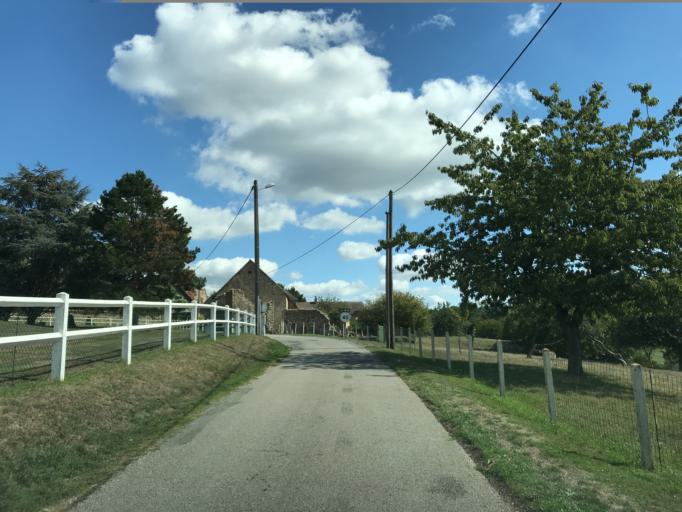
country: FR
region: Haute-Normandie
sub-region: Departement de l'Eure
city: La Chapelle-Reanville
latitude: 49.1144
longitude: 1.3749
